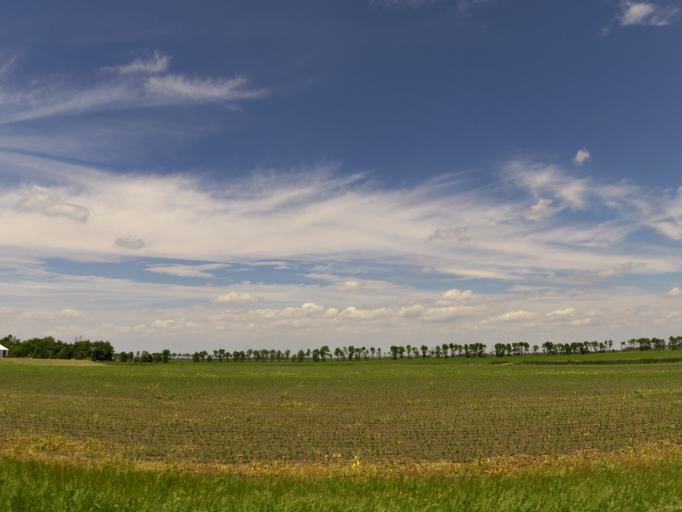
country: US
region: North Dakota
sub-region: Walsh County
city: Grafton
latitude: 48.2953
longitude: -97.2385
